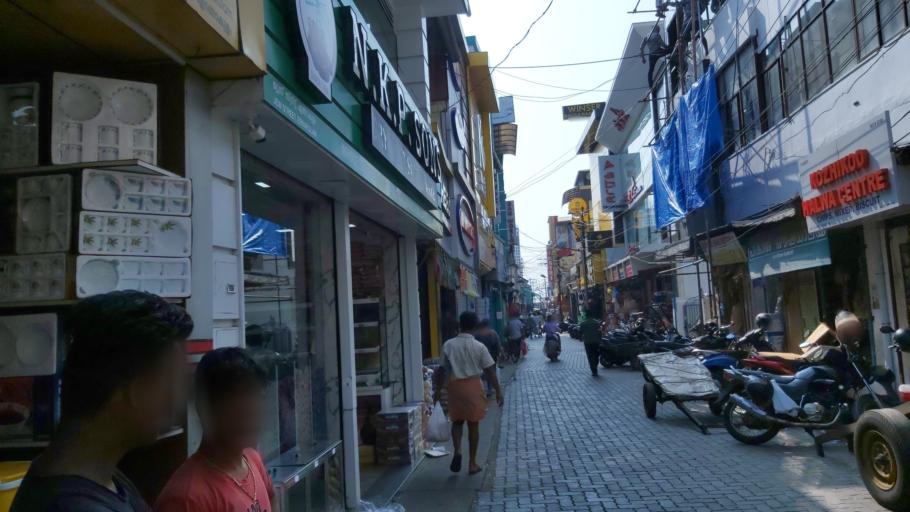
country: IN
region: Kerala
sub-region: Ernakulam
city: Cochin
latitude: 9.9804
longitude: 76.2778
